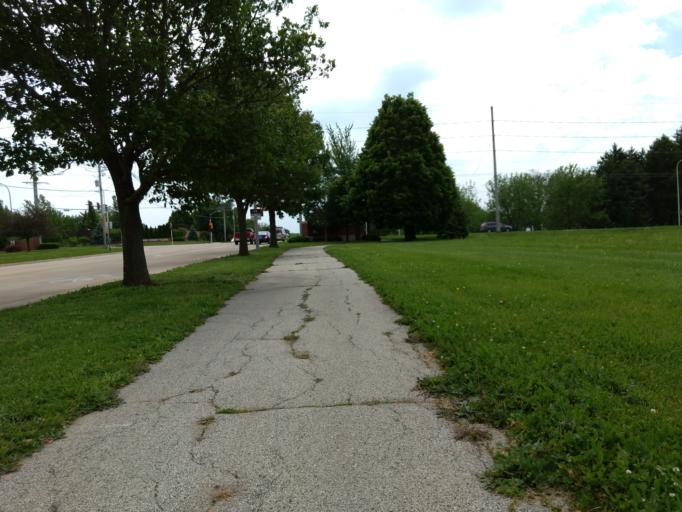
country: US
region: Illinois
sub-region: Champaign County
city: Urbana
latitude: 40.0845
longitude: -88.2096
